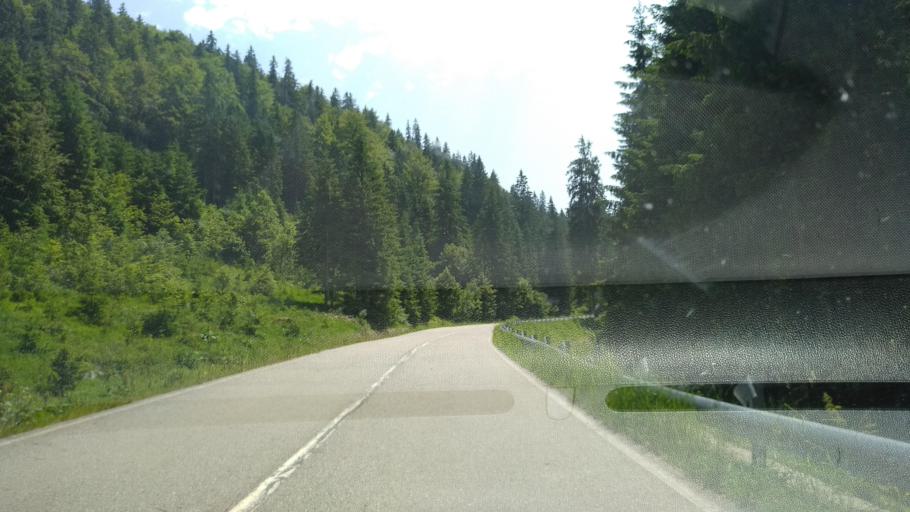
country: RO
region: Gorj
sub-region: Comuna Pades
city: Closani
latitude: 45.2596
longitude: 22.8704
